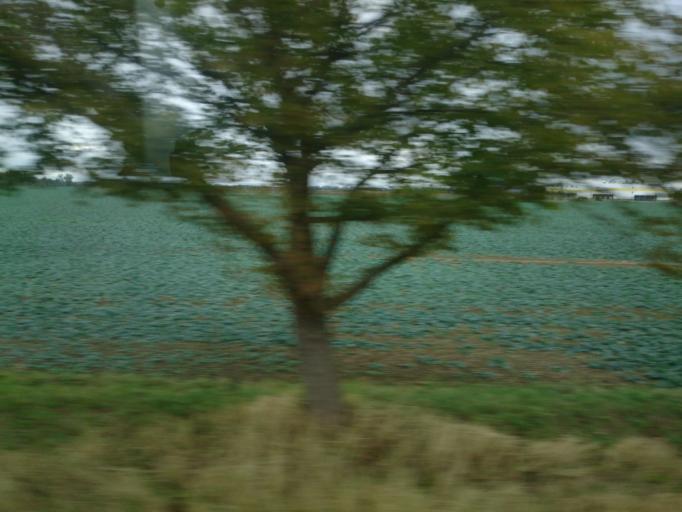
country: DE
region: Saxony-Anhalt
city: Ermlitz
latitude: 51.4030
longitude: 12.1730
